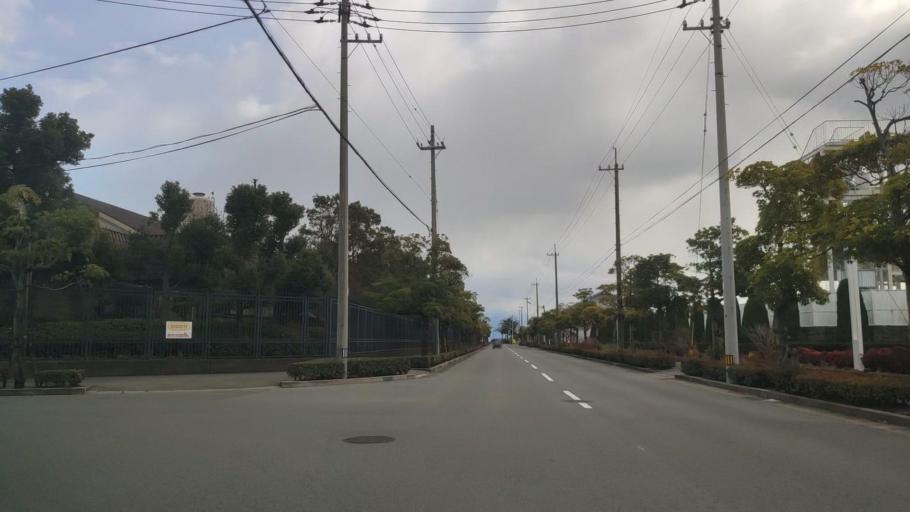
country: JP
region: Ehime
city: Saijo
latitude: 34.0479
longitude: 133.0272
